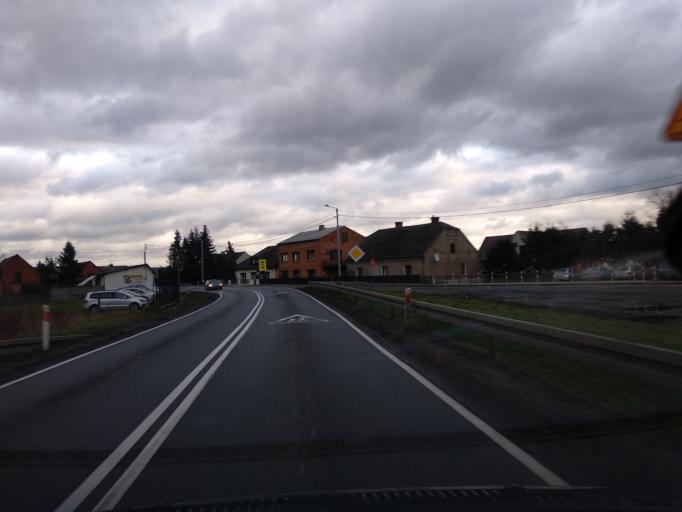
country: PL
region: Lower Silesian Voivodeship
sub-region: Powiat olesnicki
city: Miedzyborz
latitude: 51.4406
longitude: 17.7008
